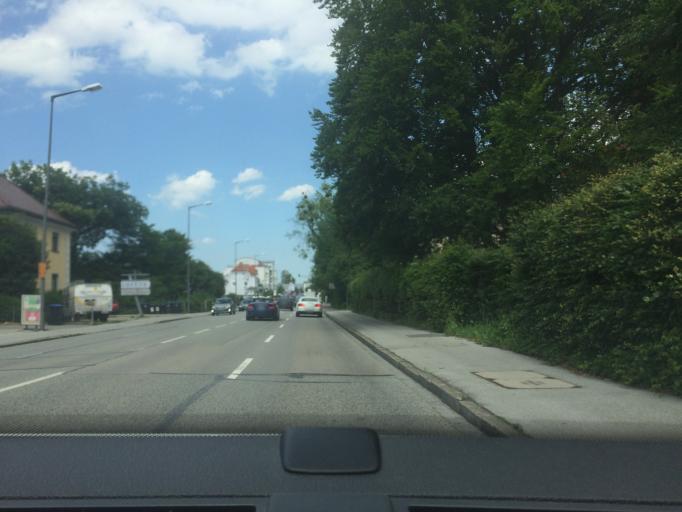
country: DE
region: Bavaria
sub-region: Upper Bavaria
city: Rosenheim
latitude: 47.8501
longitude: 12.0951
